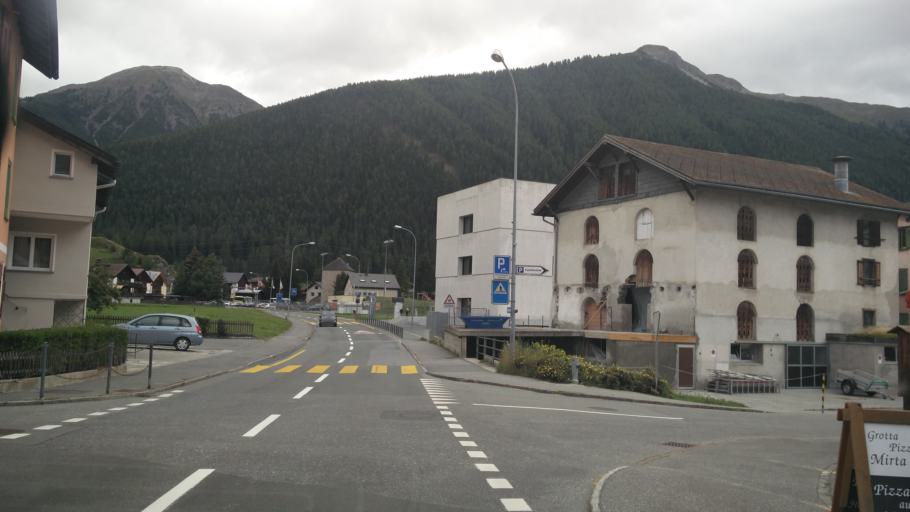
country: CH
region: Grisons
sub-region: Inn District
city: Zernez
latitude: 46.7001
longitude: 10.0952
